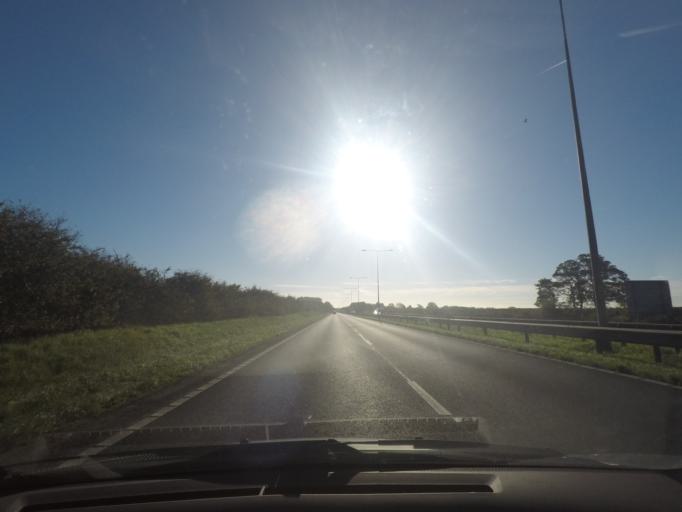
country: GB
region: England
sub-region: East Riding of Yorkshire
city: Brantingham
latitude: 53.7542
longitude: -0.5831
